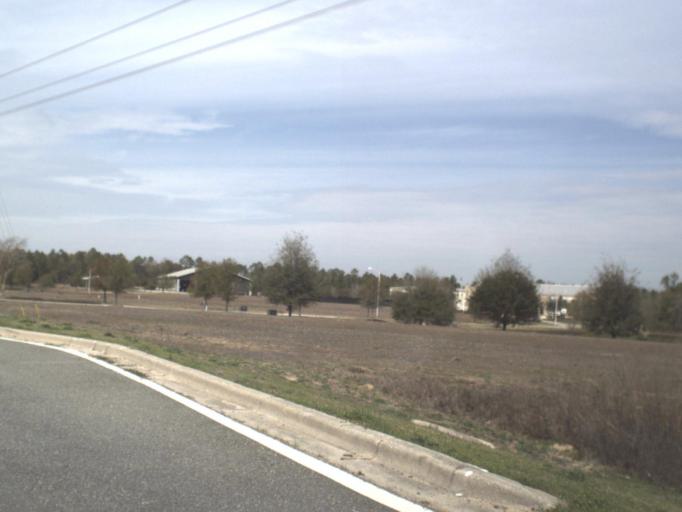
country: US
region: Florida
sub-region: Leon County
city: Tallahassee
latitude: 30.3979
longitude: -84.3280
